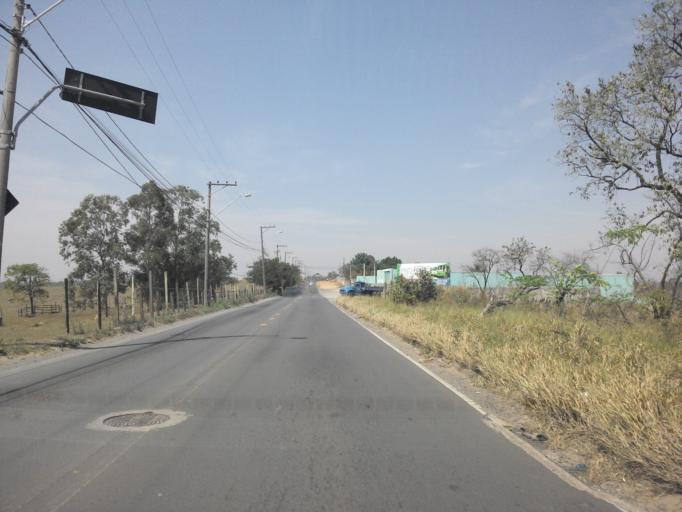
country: BR
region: Sao Paulo
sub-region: Hortolandia
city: Hortolandia
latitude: -22.9196
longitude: -47.1917
